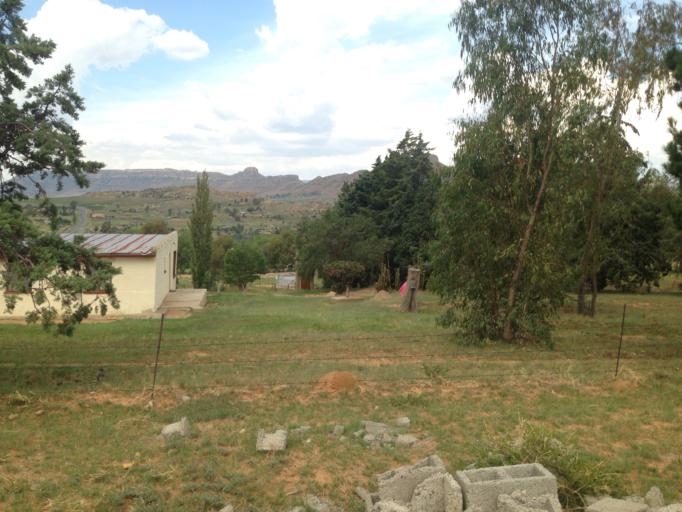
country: LS
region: Mafeteng
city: Mafeteng
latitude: -29.6932
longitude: 27.4322
